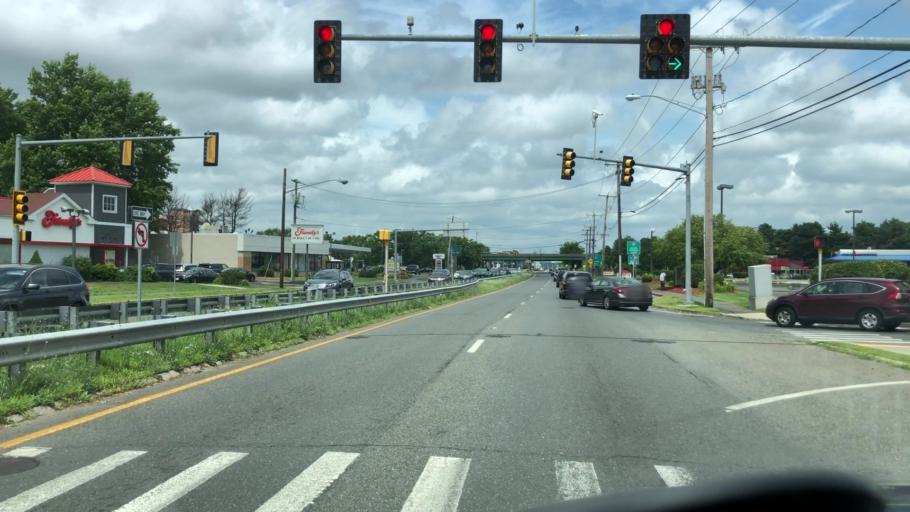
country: US
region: Massachusetts
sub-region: Hampden County
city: Chicopee
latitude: 42.1334
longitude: -72.6258
